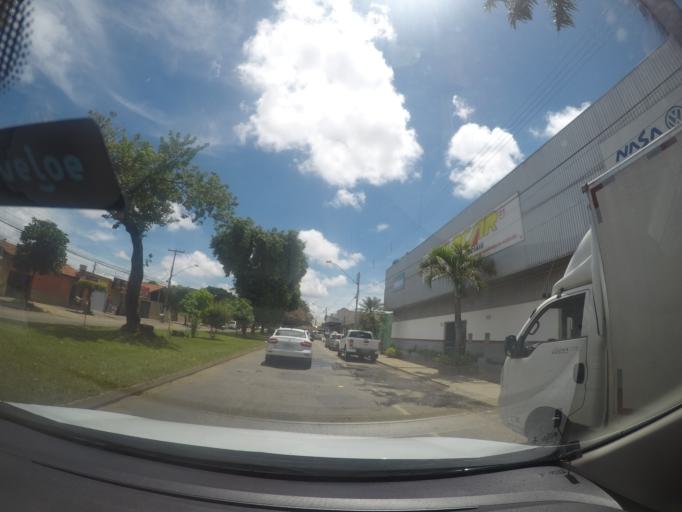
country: BR
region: Goias
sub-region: Goiania
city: Goiania
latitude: -16.6809
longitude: -49.3123
